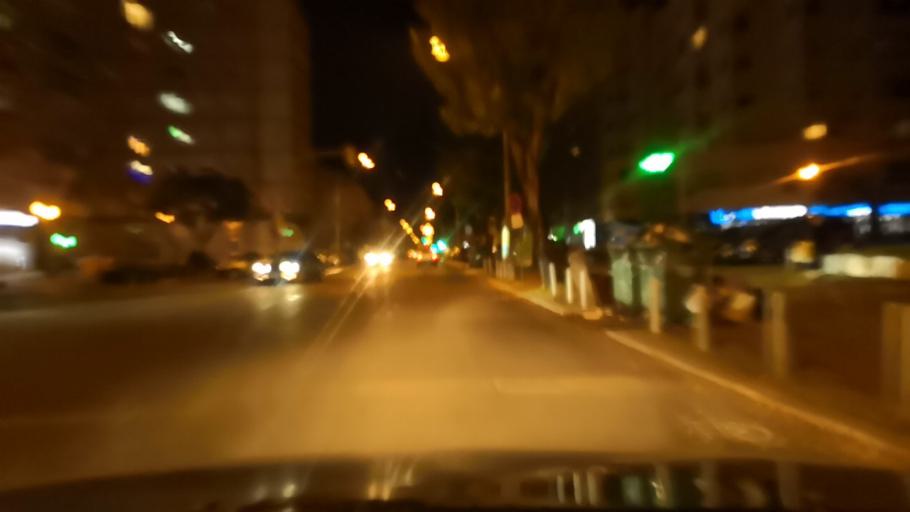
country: PT
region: Setubal
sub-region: Setubal
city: Setubal
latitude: 38.5387
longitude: -8.8948
